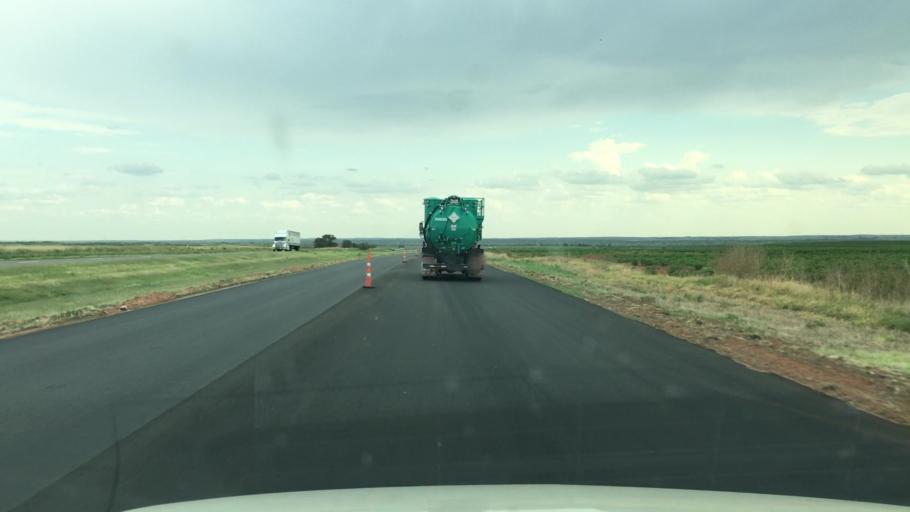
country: US
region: Texas
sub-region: Hall County
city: Memphis
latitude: 34.6136
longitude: -100.4698
